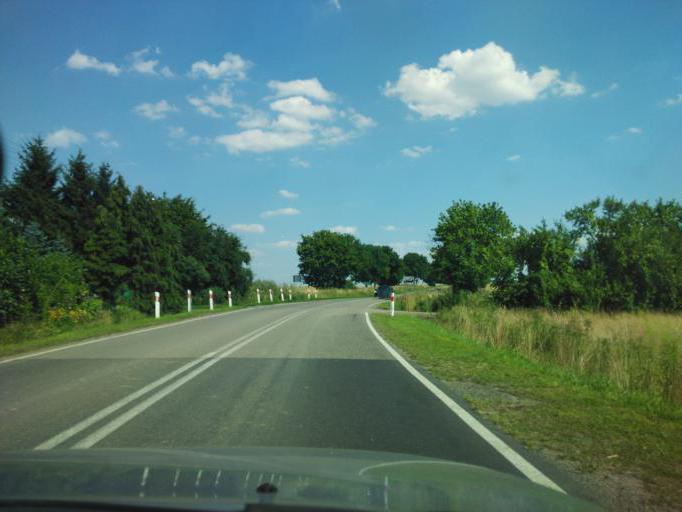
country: PL
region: West Pomeranian Voivodeship
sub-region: Powiat pyrzycki
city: Kozielice
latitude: 53.1308
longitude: 14.8342
